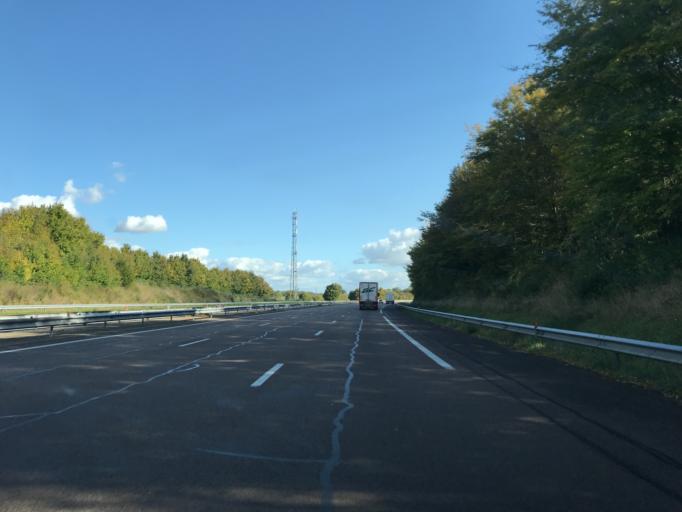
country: FR
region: Bourgogne
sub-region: Departement de l'Yonne
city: Fleury-la-Vallee
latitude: 47.8773
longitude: 3.4723
